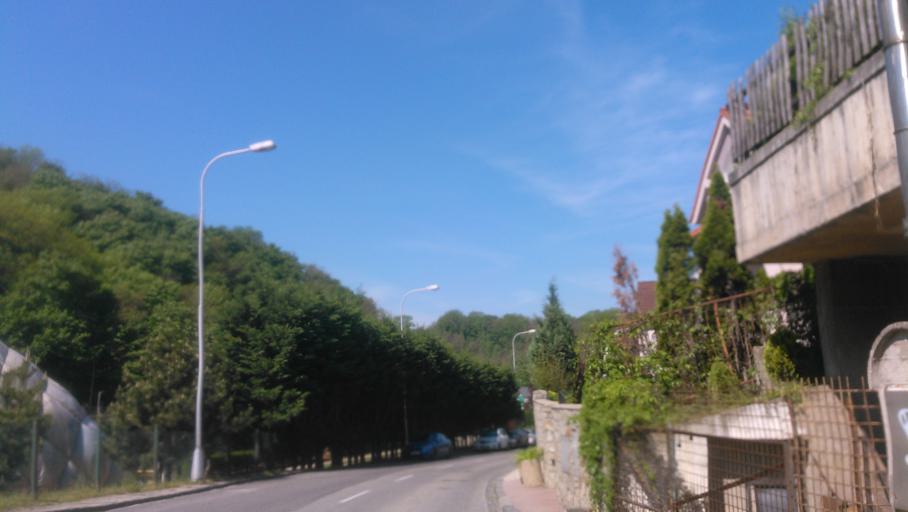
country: SK
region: Bratislavsky
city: Bratislava
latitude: 48.1641
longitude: 17.0799
